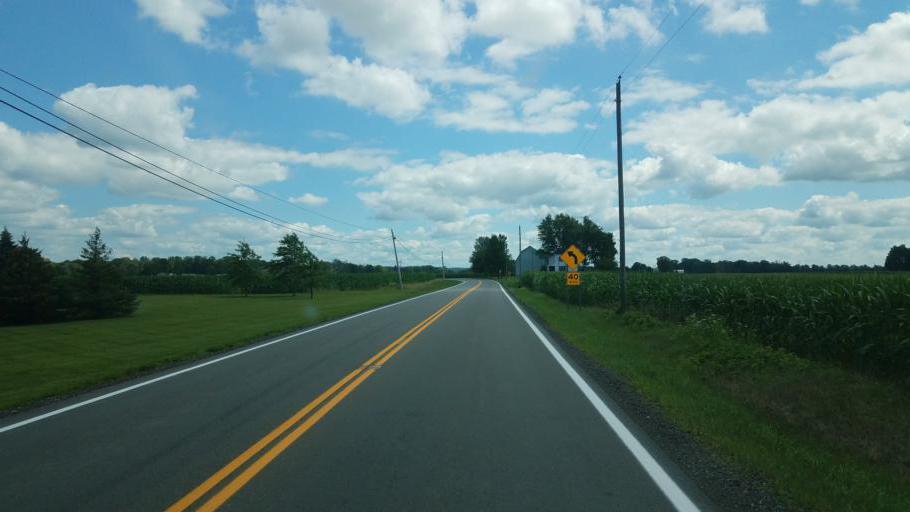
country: US
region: Ohio
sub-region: Richland County
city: Shelby
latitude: 40.8428
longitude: -82.6597
